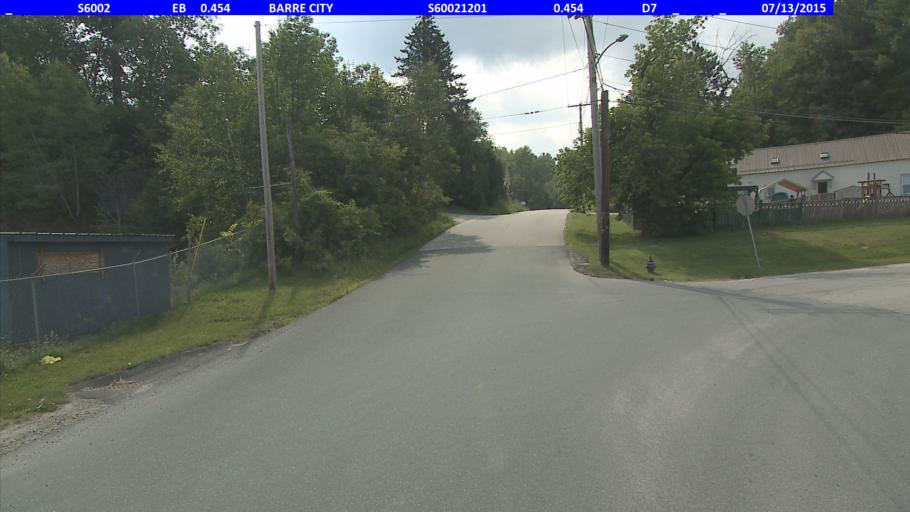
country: US
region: Vermont
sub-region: Washington County
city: Barre
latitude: 44.1884
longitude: -72.4910
